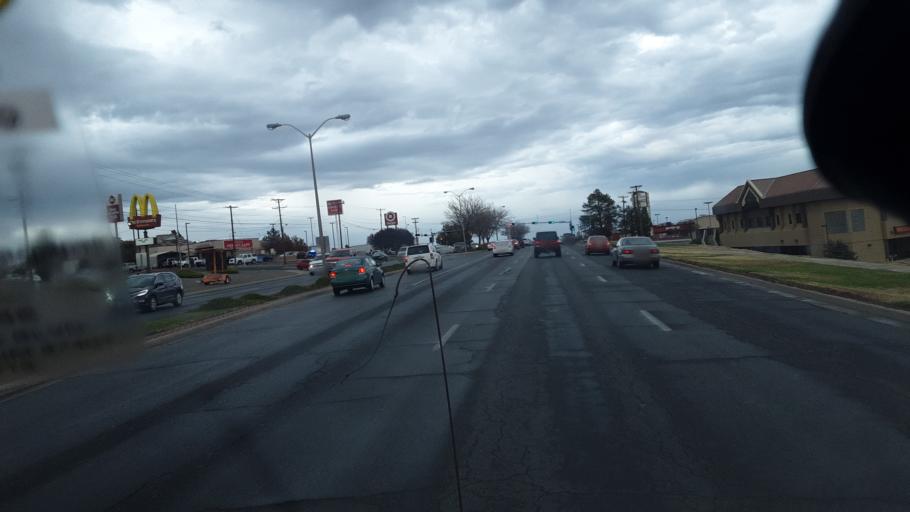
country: US
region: New Mexico
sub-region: San Juan County
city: Flora Vista
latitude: 36.7658
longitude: -108.1504
